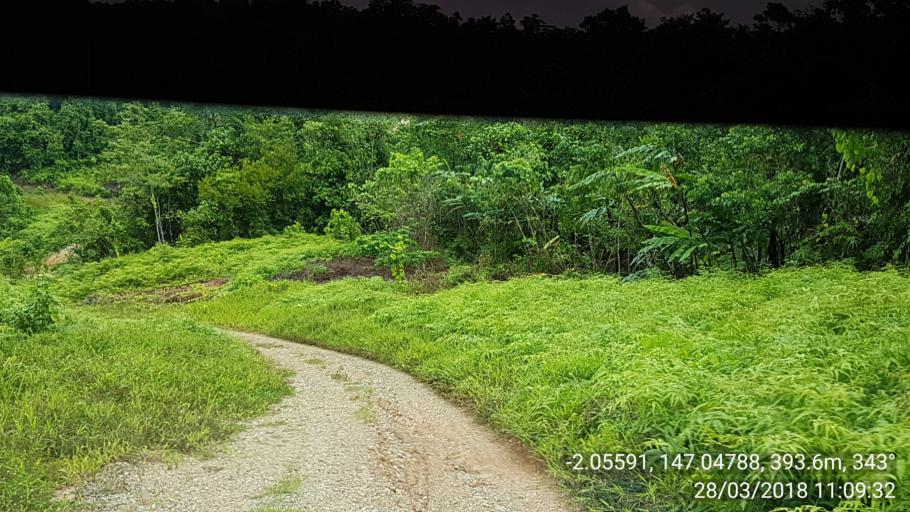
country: PG
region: Manus
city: Lorengau
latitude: -2.0561
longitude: 147.0478
